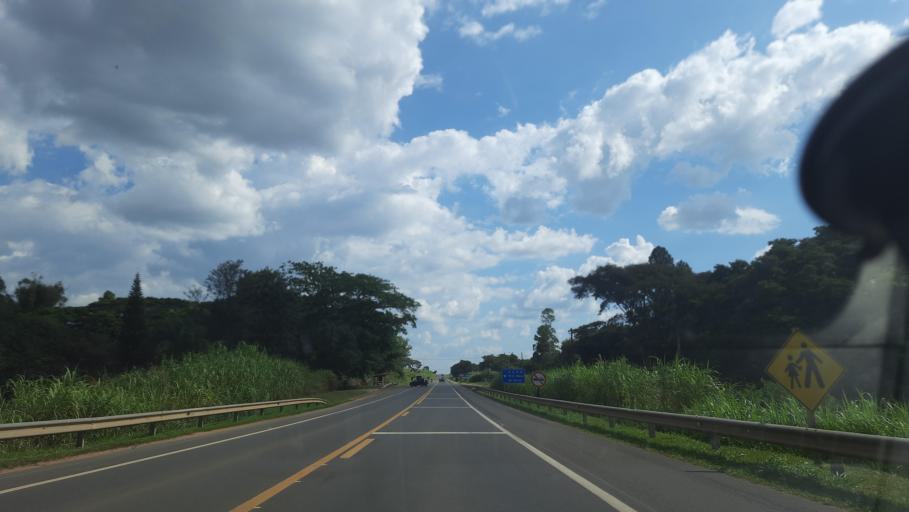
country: BR
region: Sao Paulo
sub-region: Sao Jose Do Rio Pardo
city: Sao Jose do Rio Pardo
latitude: -21.6675
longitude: -46.9207
